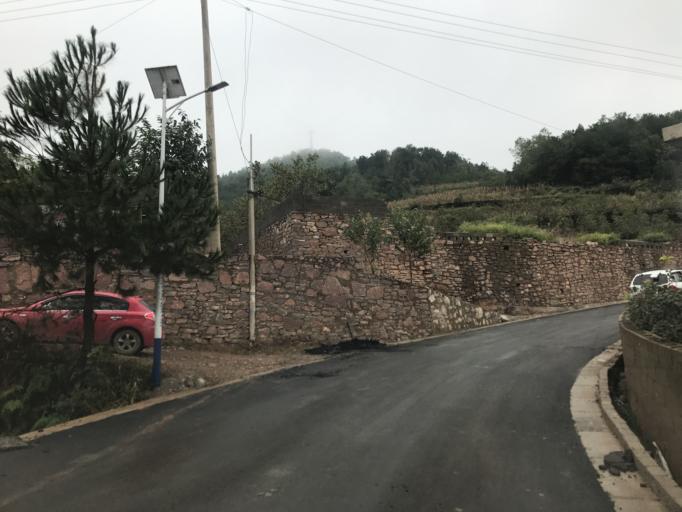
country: CN
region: Guizhou Sheng
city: Supu
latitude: 26.7365
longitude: 106.4375
